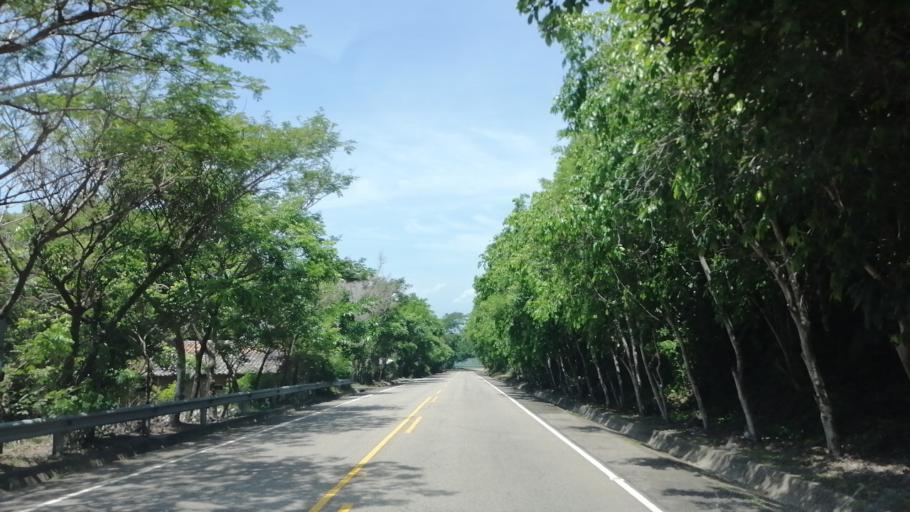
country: SV
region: Chalatenango
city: Nueva Concepcion
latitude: 14.1661
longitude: -89.3097
